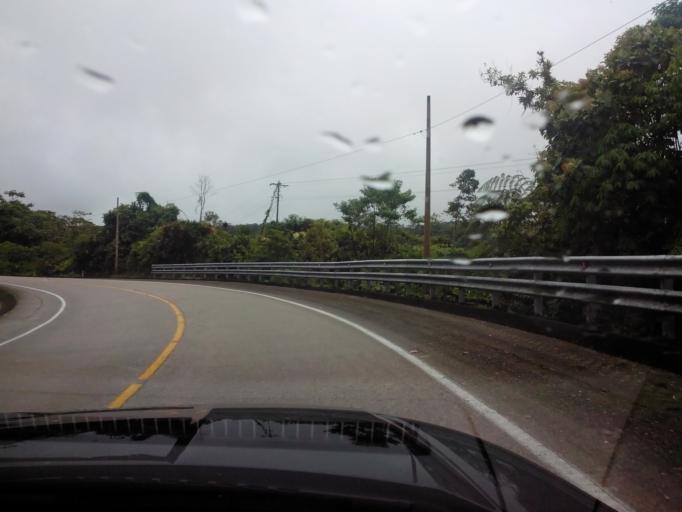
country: EC
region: Napo
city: Archidona
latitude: -0.7862
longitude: -77.7803
